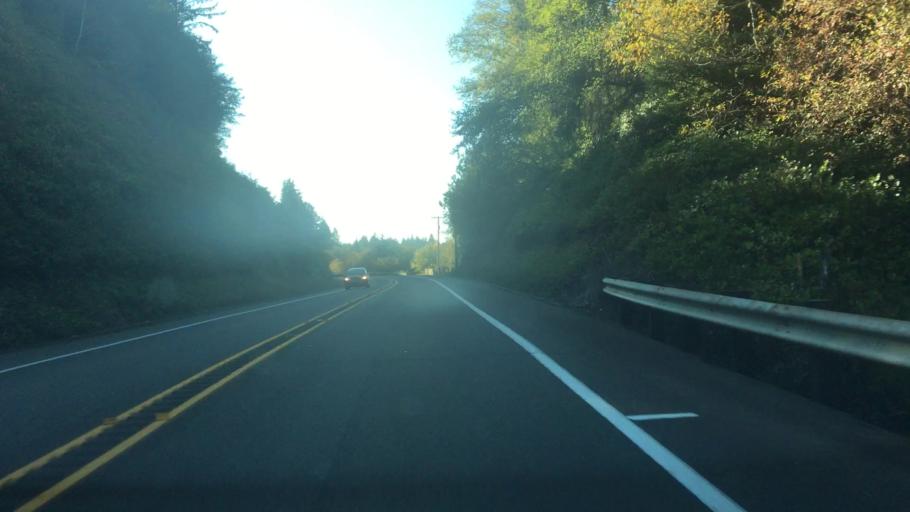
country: US
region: Washington
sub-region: Pacific County
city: South Bend
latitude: 46.6794
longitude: -123.8993
